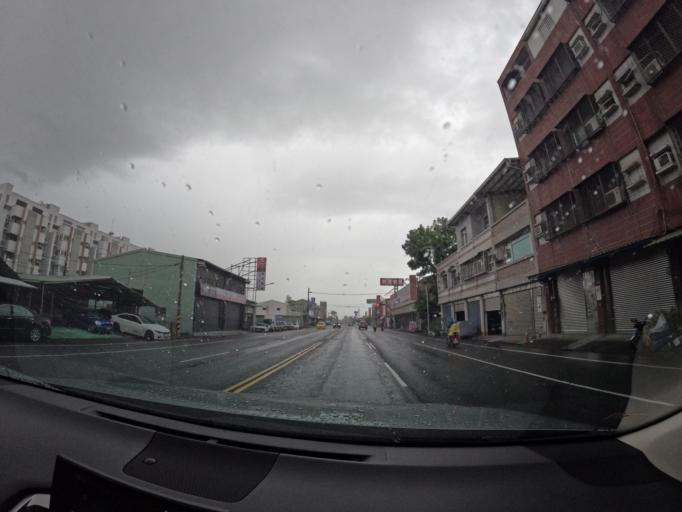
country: TW
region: Taiwan
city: Fengshan
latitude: 22.6504
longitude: 120.3654
